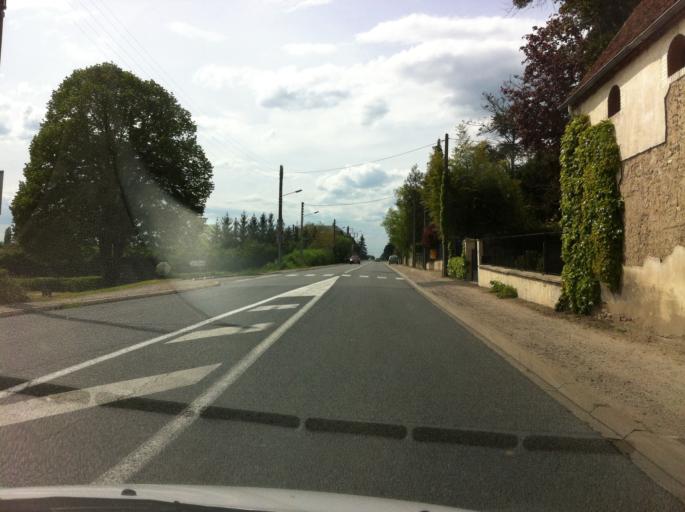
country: FR
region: Auvergne
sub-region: Departement de l'Allier
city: Saint-Pourcain-sur-Sioule
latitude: 46.3113
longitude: 3.2821
